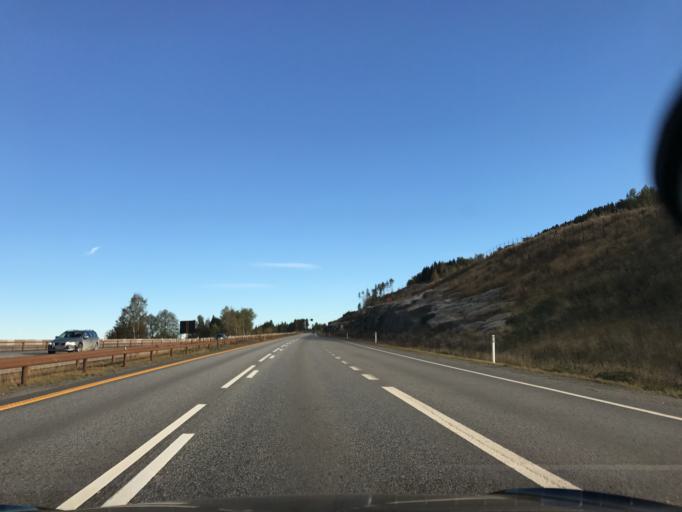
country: NO
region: Hedmark
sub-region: Stange
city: Stange
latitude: 60.5658
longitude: 11.2577
